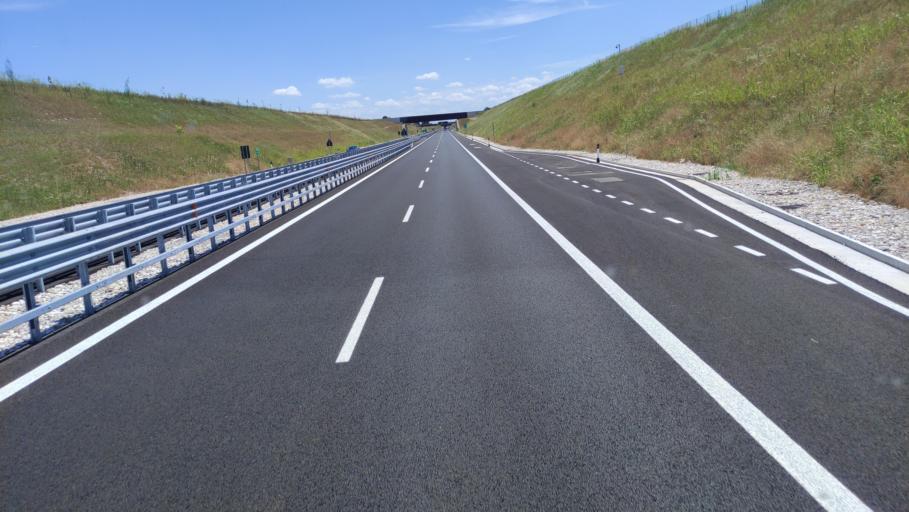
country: IT
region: Veneto
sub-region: Provincia di Treviso
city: Riese Pio X
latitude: 45.7424
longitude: 11.9351
